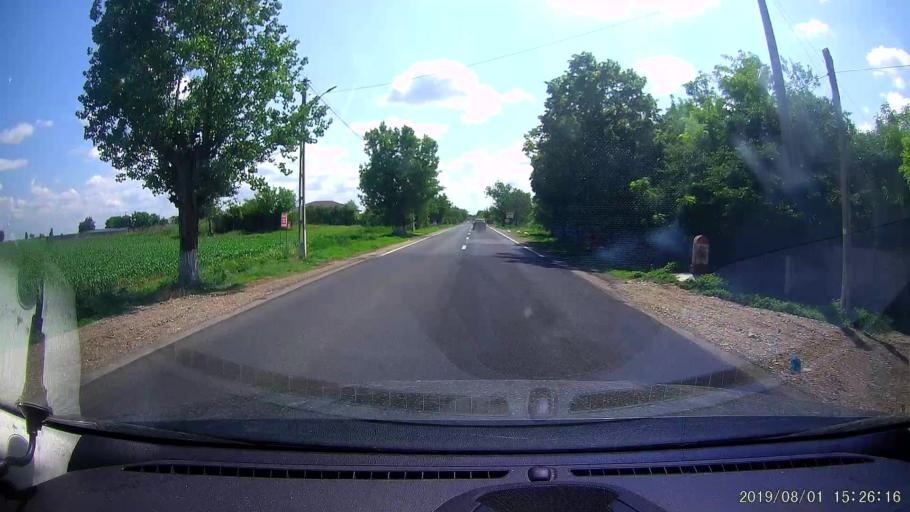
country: RO
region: Braila
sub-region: Comuna Viziru
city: Viziru
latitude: 45.0116
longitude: 27.7229
